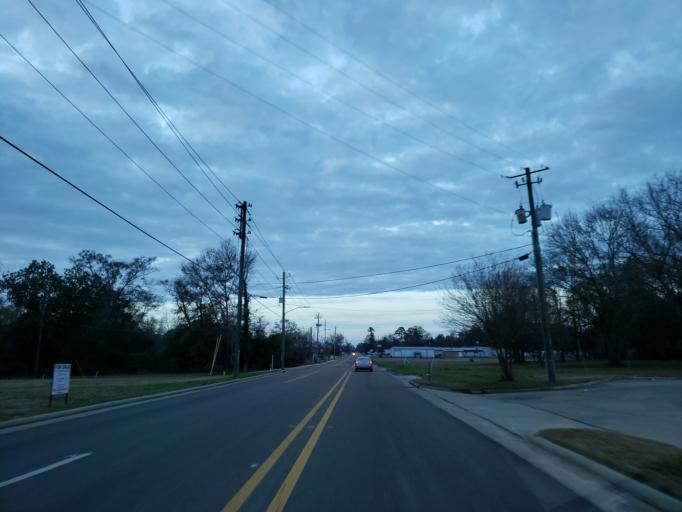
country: US
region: Mississippi
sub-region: Forrest County
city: Petal
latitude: 31.3314
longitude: -89.2629
